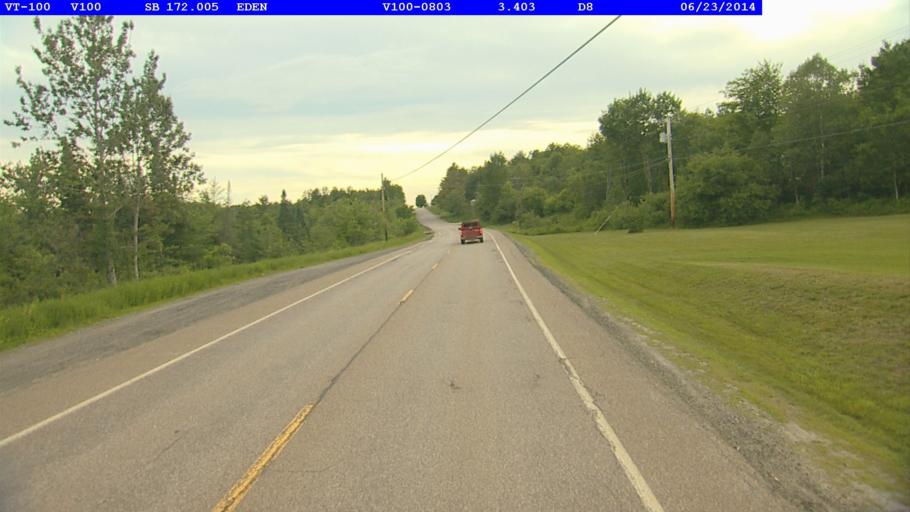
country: US
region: Vermont
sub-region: Lamoille County
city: Hyde Park
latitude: 44.7107
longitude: -72.5364
